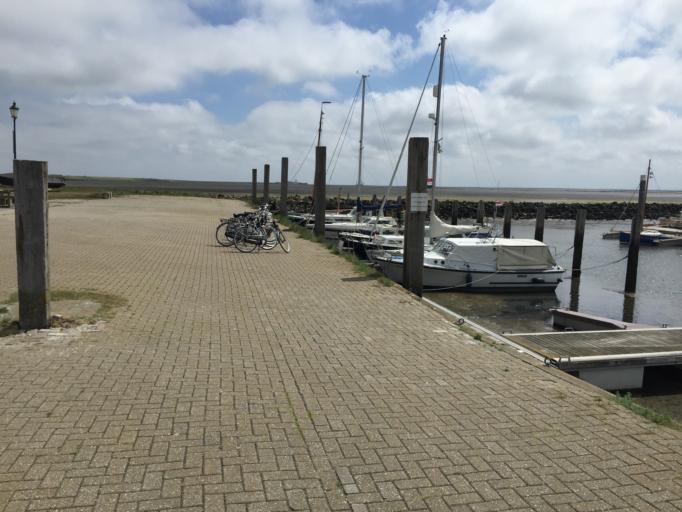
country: NL
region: Friesland
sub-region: Gemeente Schiermonnikoog
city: Schiermonnikoog
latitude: 53.4702
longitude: 6.1664
